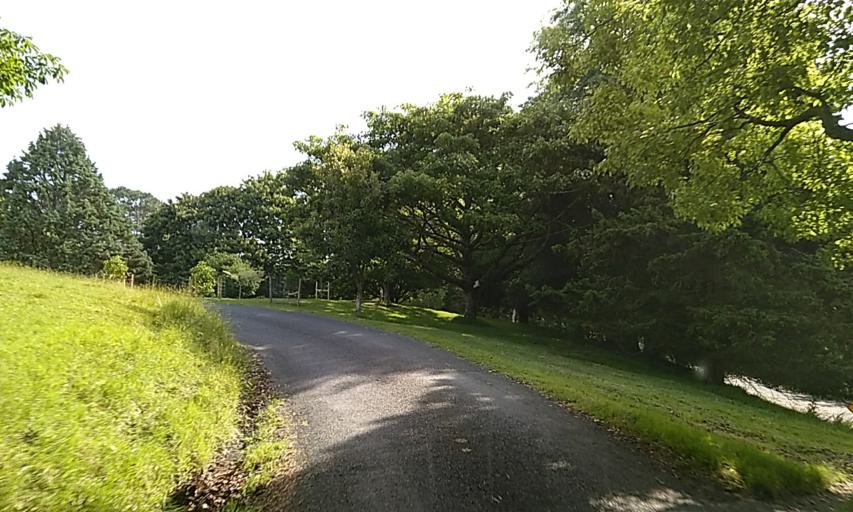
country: NZ
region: Bay of Plenty
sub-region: Tauranga City
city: Tauranga
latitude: -37.8142
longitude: 176.0437
